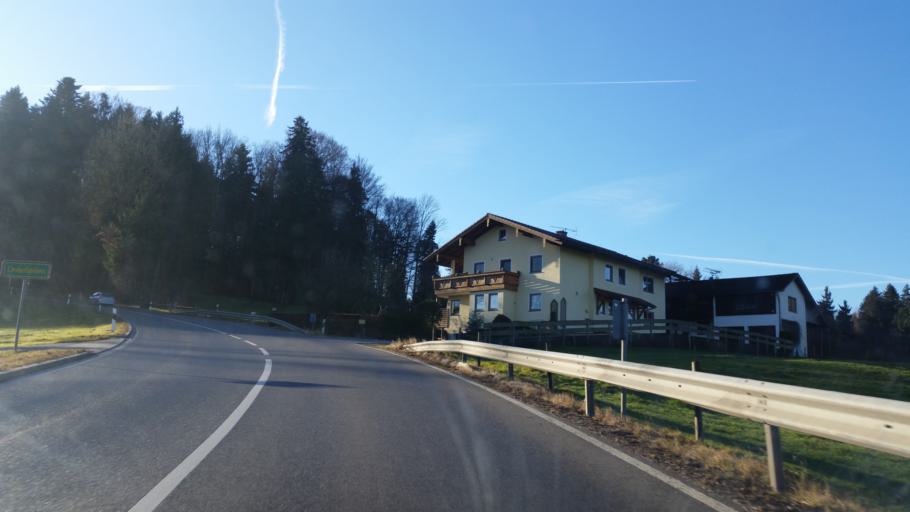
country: DE
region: Bavaria
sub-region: Upper Bavaria
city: Irschenberg
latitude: 47.8567
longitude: 11.9333
